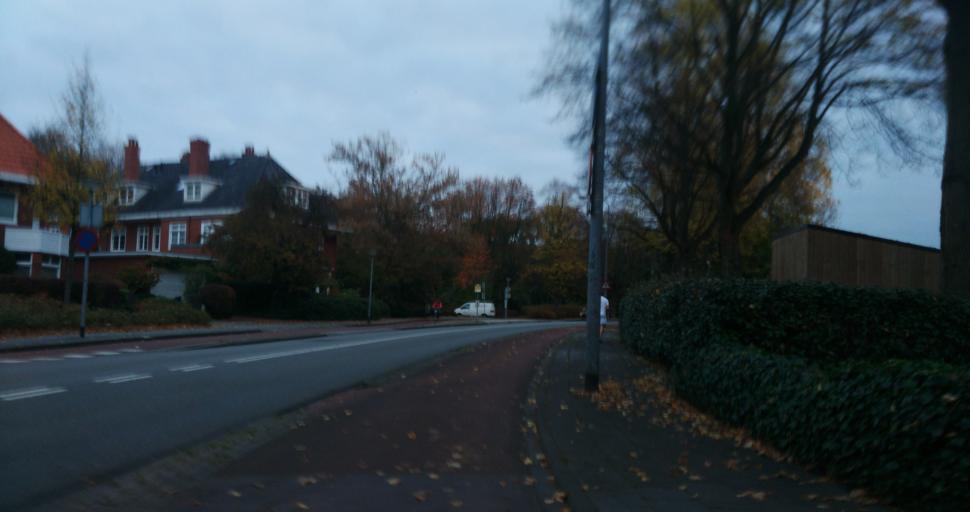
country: NL
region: Groningen
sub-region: Gemeente Groningen
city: Groningen
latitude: 53.2198
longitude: 6.5521
